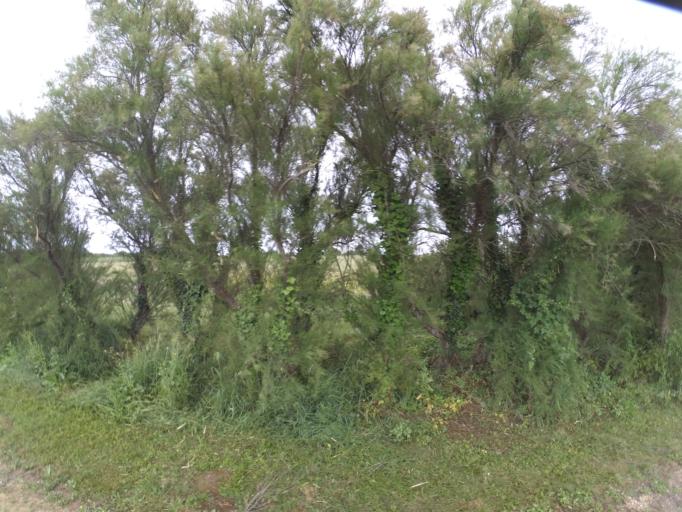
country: FR
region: Poitou-Charentes
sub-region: Departement de la Charente-Maritime
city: Aytre
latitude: 46.1306
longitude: -1.1315
